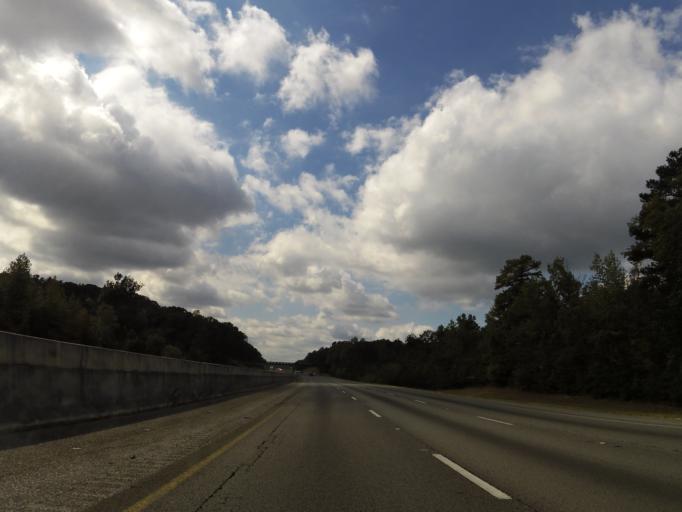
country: US
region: Alabama
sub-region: Tuscaloosa County
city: Lake View
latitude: 33.3041
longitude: -87.0685
